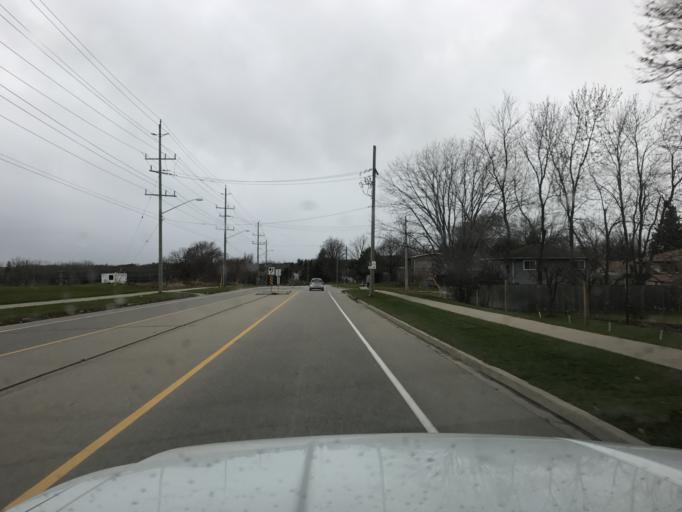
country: CA
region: Ontario
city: Waterloo
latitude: 43.4839
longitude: -80.5592
